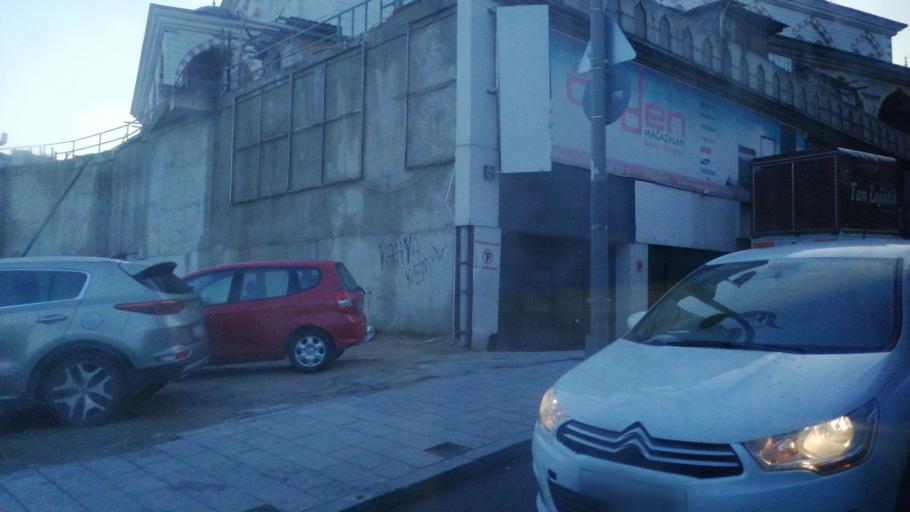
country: TR
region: Istanbul
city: Sisli
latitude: 41.0853
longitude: 28.9874
